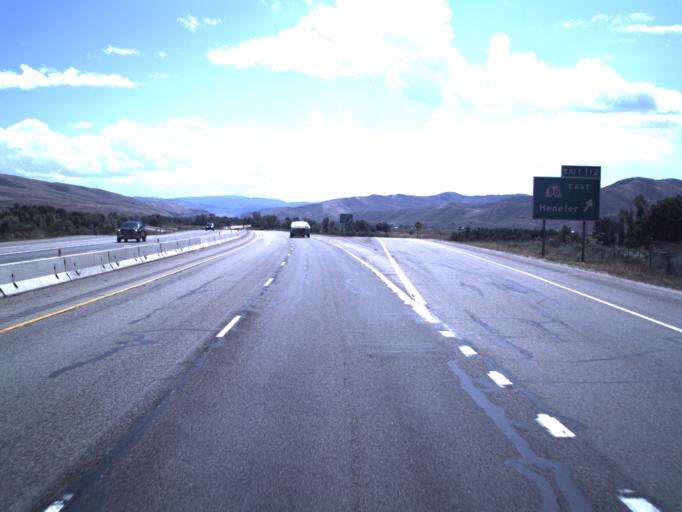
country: US
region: Utah
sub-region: Morgan County
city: Morgan
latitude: 41.0471
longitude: -111.5264
